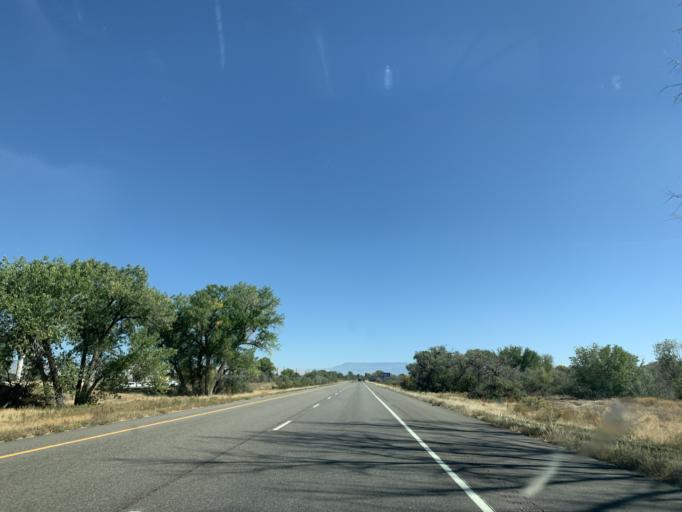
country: US
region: Colorado
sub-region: Mesa County
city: Fruita
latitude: 39.1617
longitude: -108.7682
